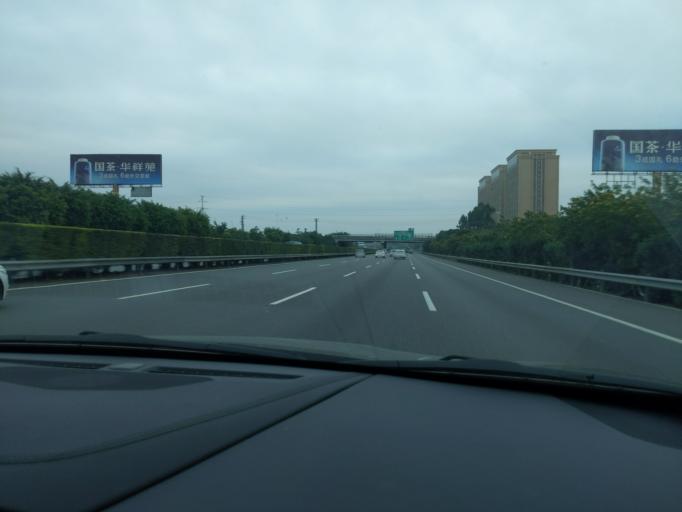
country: CN
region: Fujian
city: Neikeng
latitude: 24.7799
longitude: 118.4653
